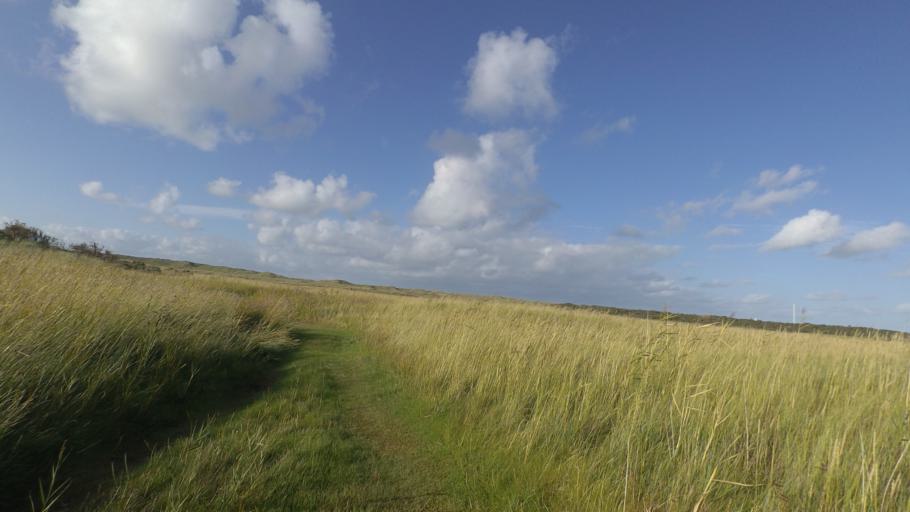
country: NL
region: Friesland
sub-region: Gemeente Dongeradeel
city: Ternaard
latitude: 53.4620
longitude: 5.9173
